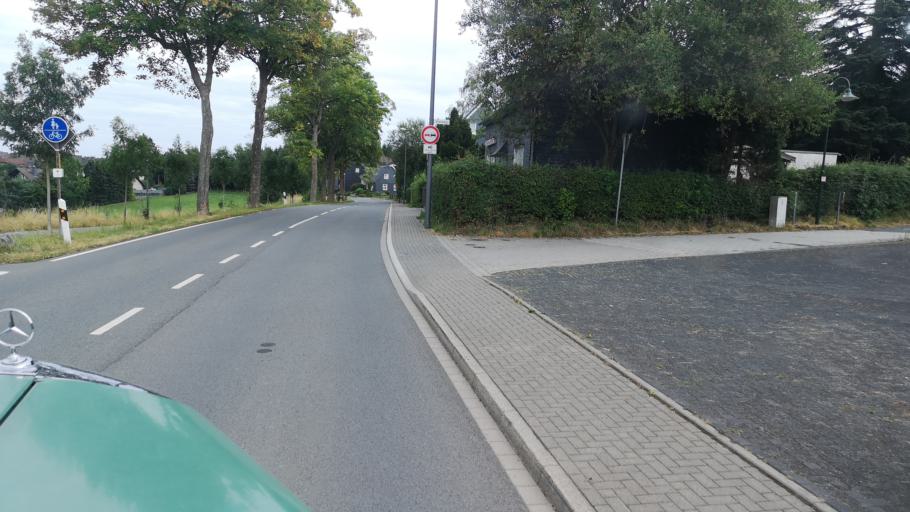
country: DE
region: North Rhine-Westphalia
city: Wermelskirchen
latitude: 51.0996
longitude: 7.2132
